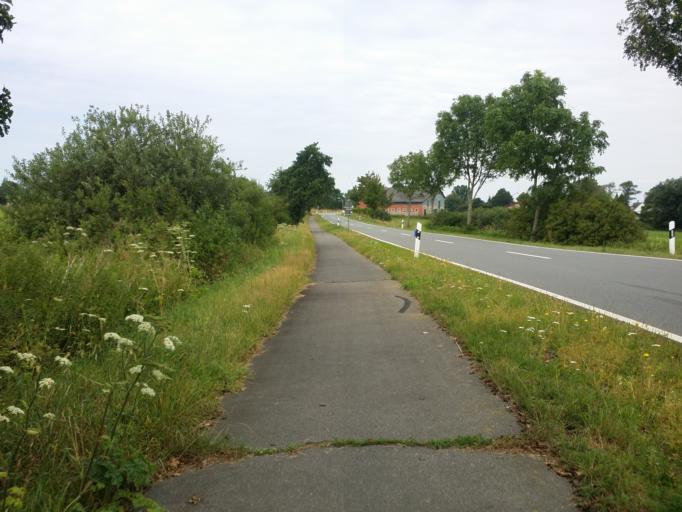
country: DE
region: Schleswig-Holstein
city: Huje
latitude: 53.9714
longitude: 9.4419
